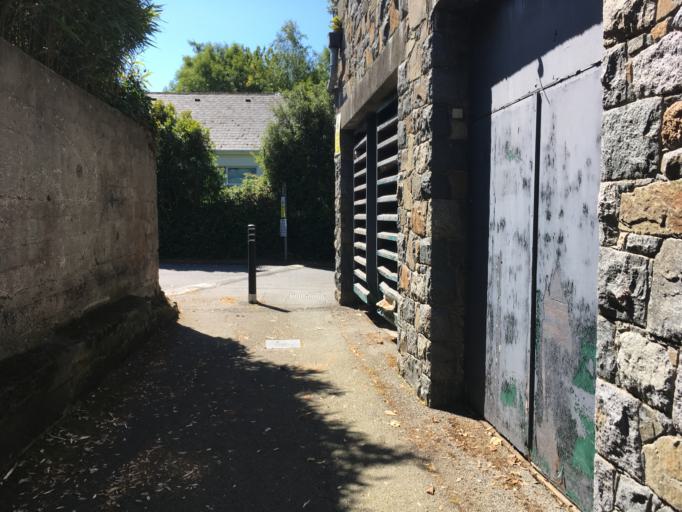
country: GG
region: St Peter Port
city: Saint Peter Port
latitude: 49.4606
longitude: -2.5597
